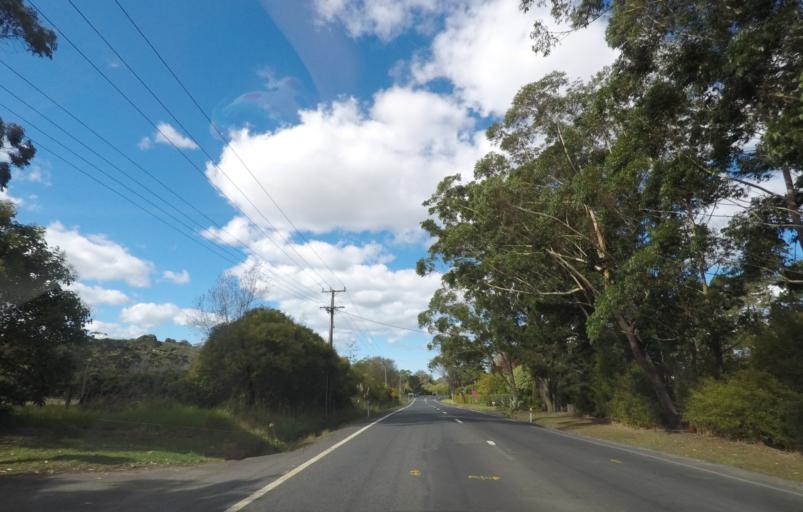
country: NZ
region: Auckland
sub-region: Auckland
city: Rothesay Bay
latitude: -36.5985
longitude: 174.6549
